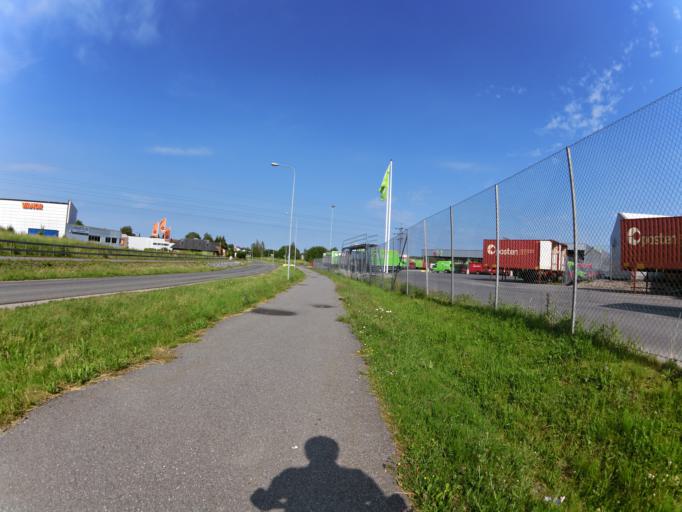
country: NO
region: Ostfold
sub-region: Fredrikstad
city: Fredrikstad
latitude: 59.2397
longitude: 10.9926
